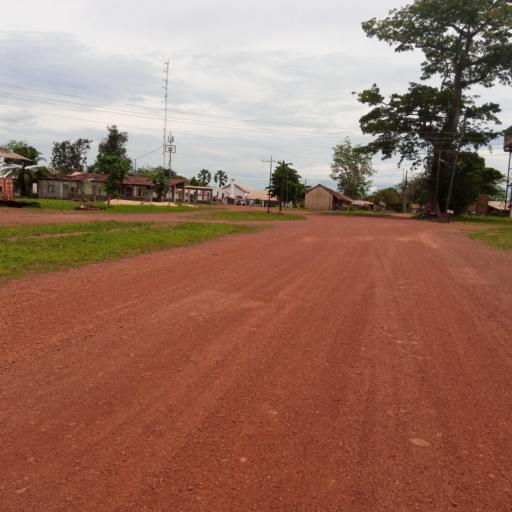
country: SL
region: Southern Province
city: Largo
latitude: 8.1106
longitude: -12.0779
